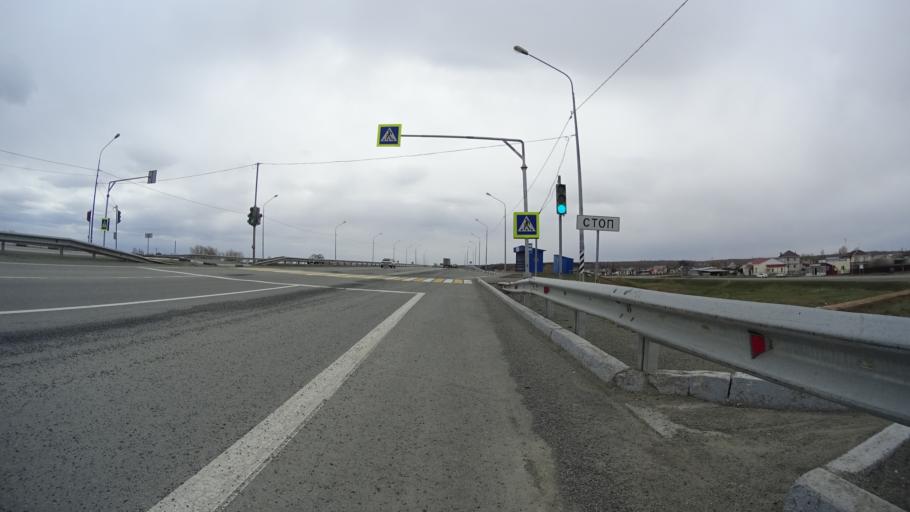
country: RU
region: Chelyabinsk
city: Yemanzhelinka
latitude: 54.7967
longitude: 61.3067
